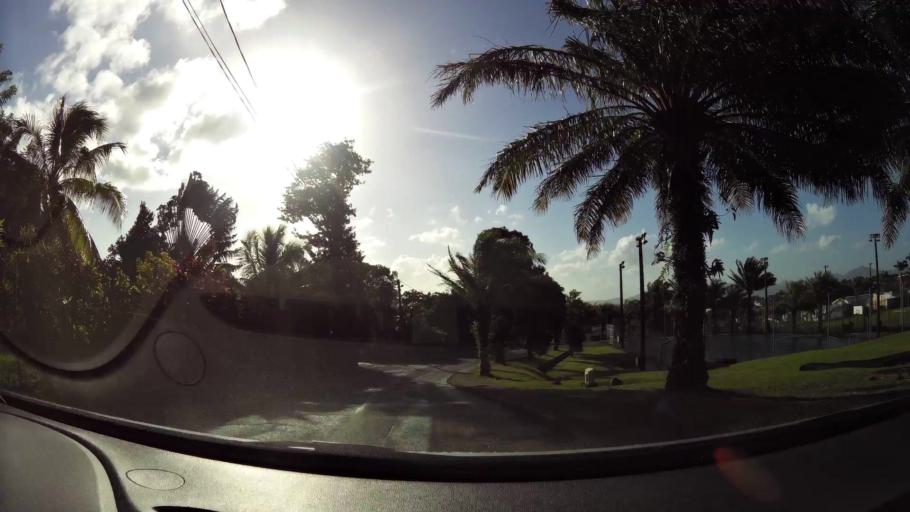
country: MQ
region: Martinique
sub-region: Martinique
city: Le Lamentin
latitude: 14.6240
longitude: -61.0242
